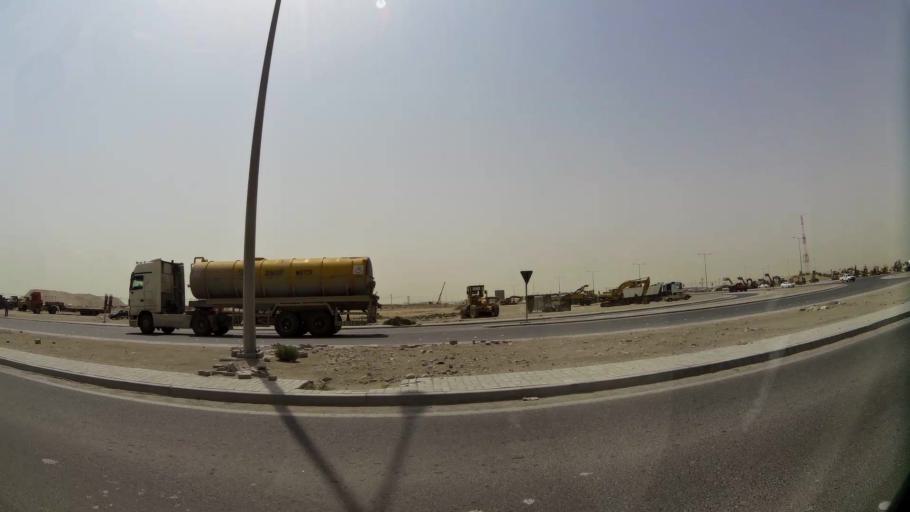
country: QA
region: Baladiyat ar Rayyan
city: Ar Rayyan
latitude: 25.1789
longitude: 51.3991
